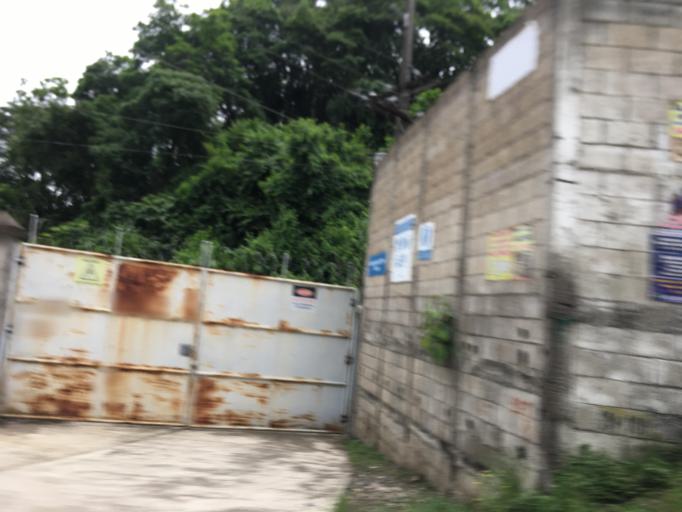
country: GT
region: Guatemala
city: Amatitlan
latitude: 14.4614
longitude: -90.5807
